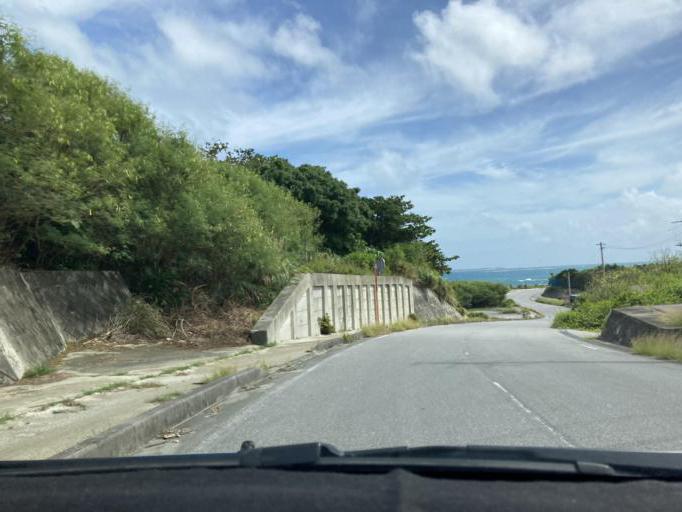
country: JP
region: Okinawa
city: Ginowan
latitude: 26.1875
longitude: 127.8205
